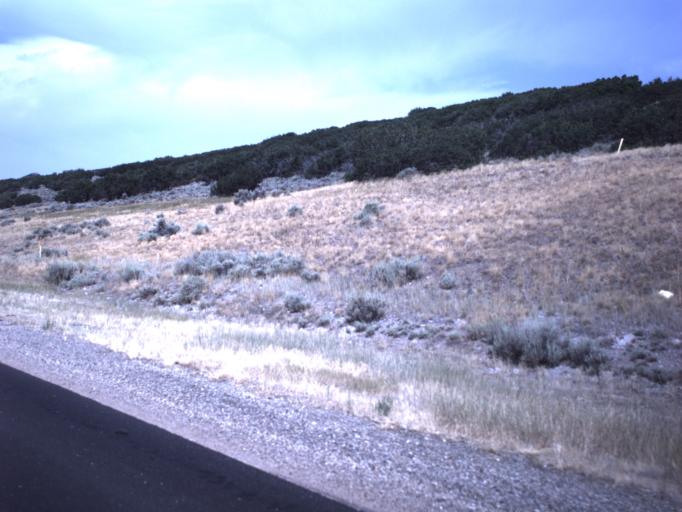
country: US
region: Utah
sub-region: Summit County
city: Kamas
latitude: 40.6339
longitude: -111.3492
